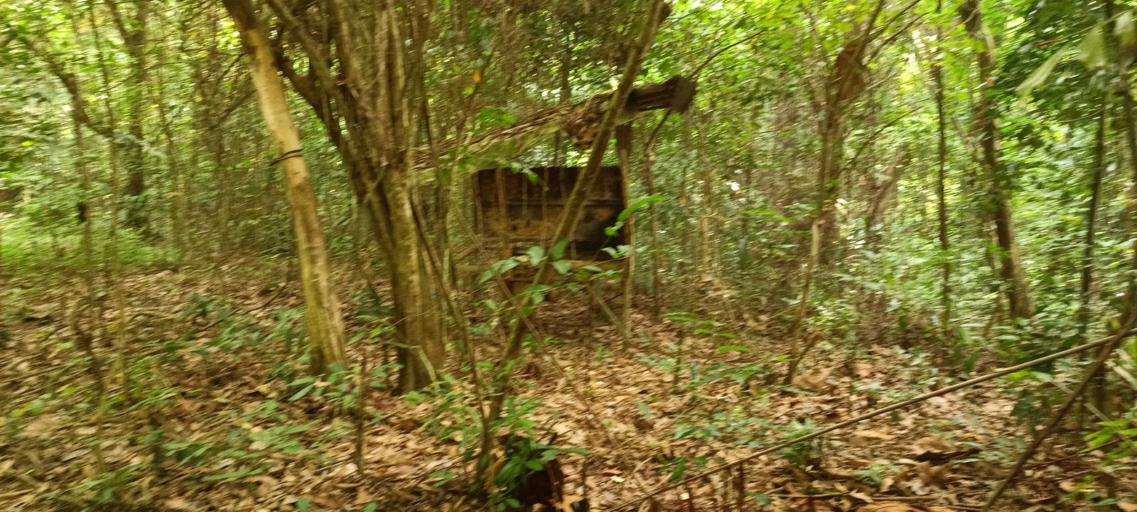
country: MY
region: Penang
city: George Town
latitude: 5.3952
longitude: 100.2930
